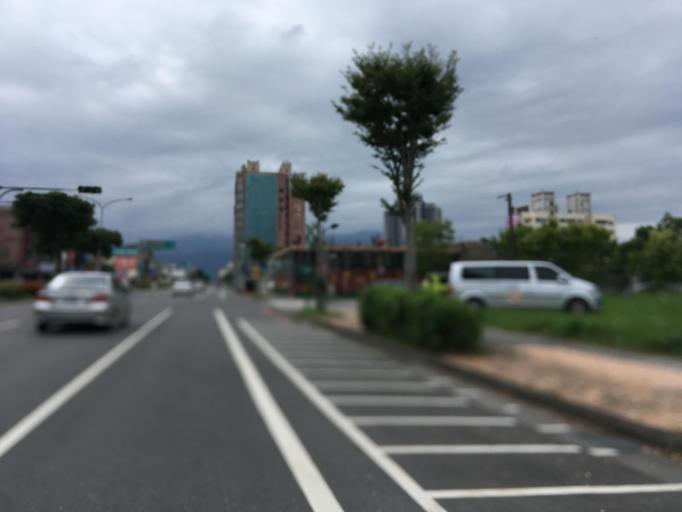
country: TW
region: Taiwan
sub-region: Yilan
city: Yilan
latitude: 24.6795
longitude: 121.7777
